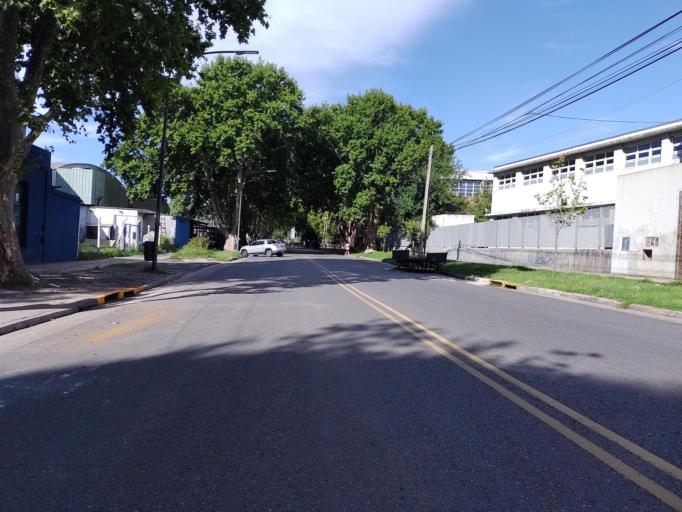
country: AR
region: Buenos Aires F.D.
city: Colegiales
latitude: -34.5434
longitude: -58.4570
